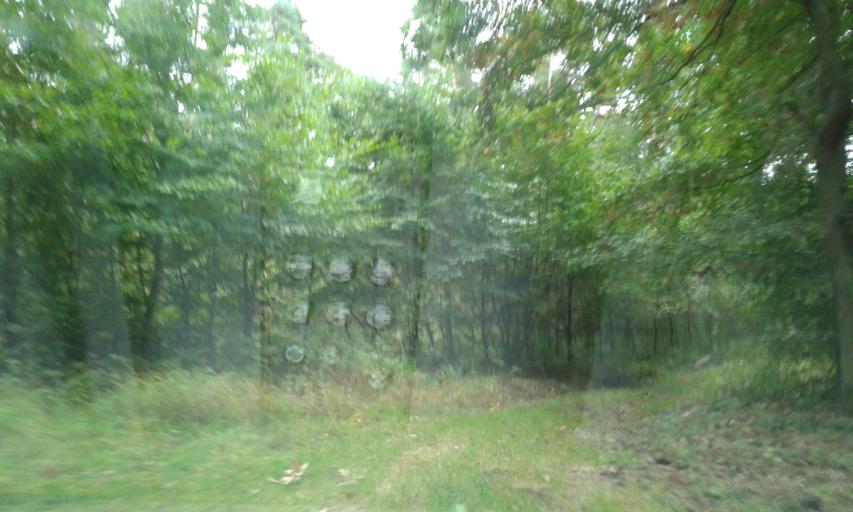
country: PL
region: West Pomeranian Voivodeship
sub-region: Powiat choszczenski
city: Pelczyce
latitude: 53.0826
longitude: 15.2642
